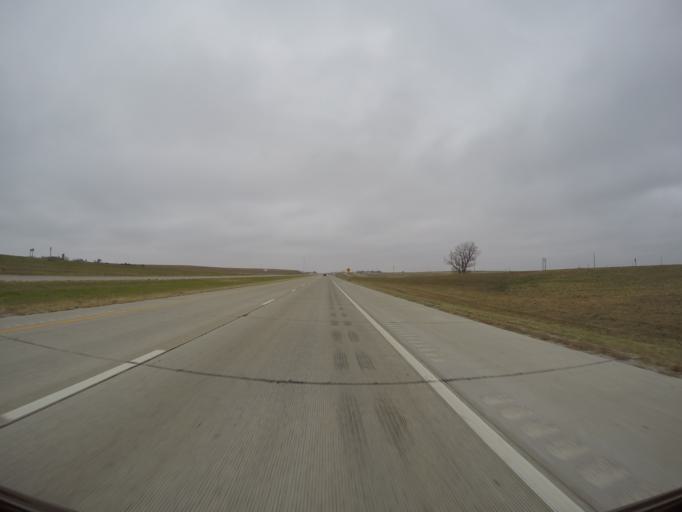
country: US
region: Kansas
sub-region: Dickinson County
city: Abilene
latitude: 38.9440
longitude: -97.1679
